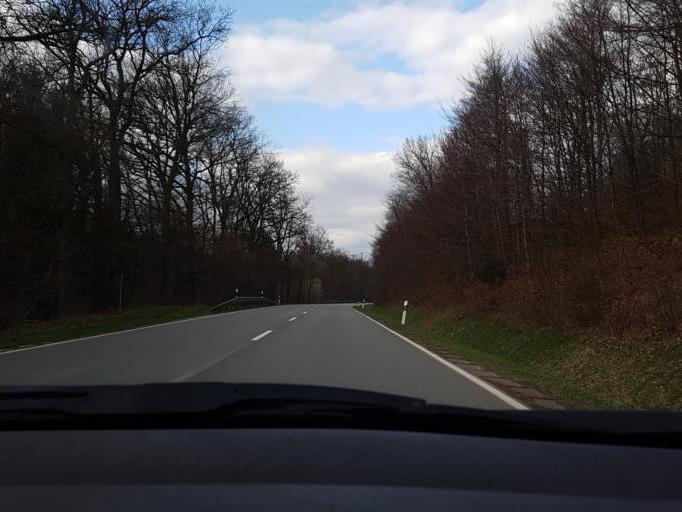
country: DE
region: Lower Saxony
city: Derental
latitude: 51.7321
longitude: 9.5128
